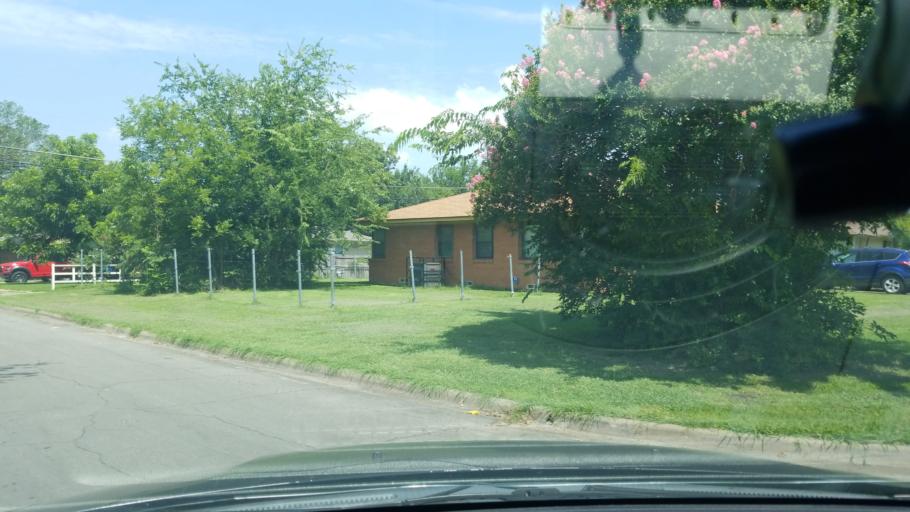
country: US
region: Texas
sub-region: Dallas County
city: Balch Springs
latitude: 32.7471
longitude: -96.6866
